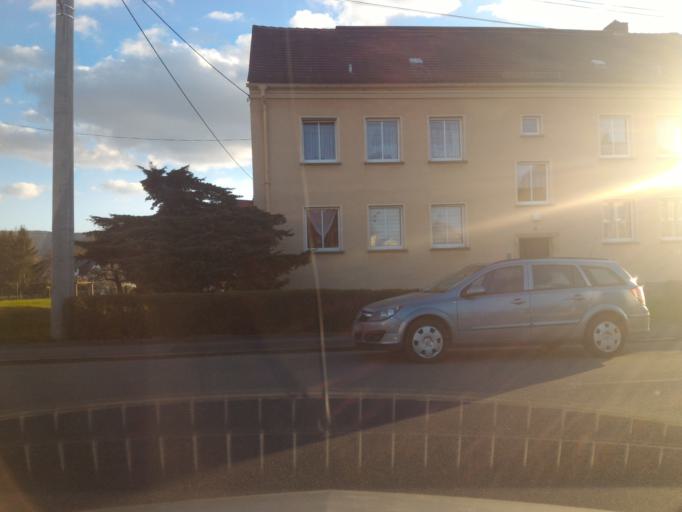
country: DE
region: Saxony
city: Grossschonau
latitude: 50.8880
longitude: 14.6624
